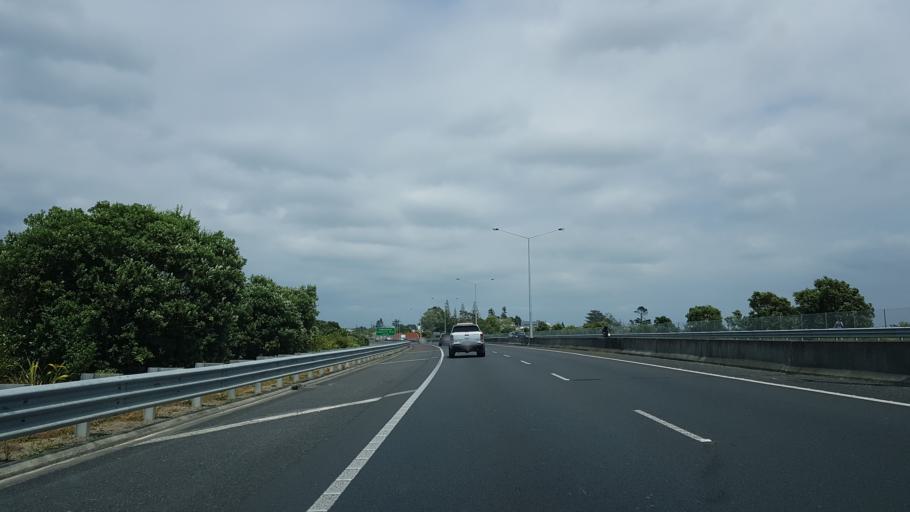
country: NZ
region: Auckland
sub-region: Auckland
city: North Shore
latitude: -36.7861
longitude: 174.6635
